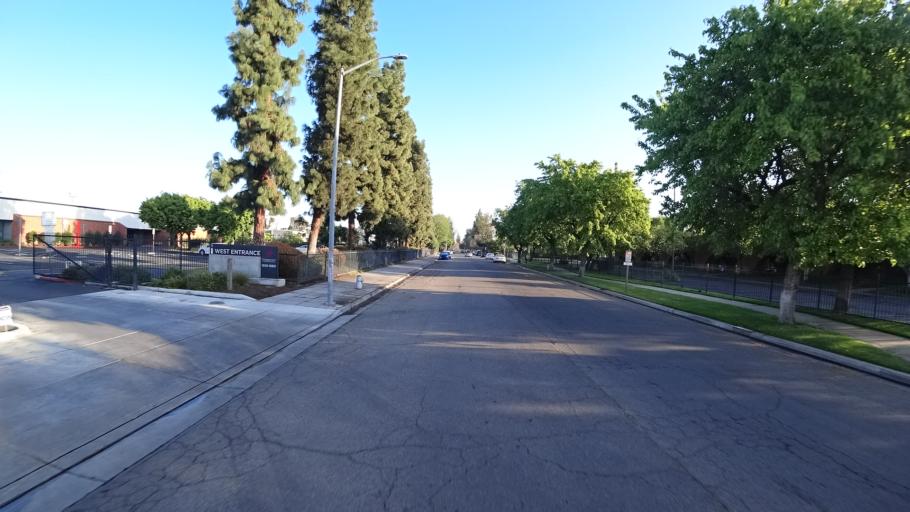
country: US
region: California
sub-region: Fresno County
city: Clovis
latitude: 36.8094
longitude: -119.7587
